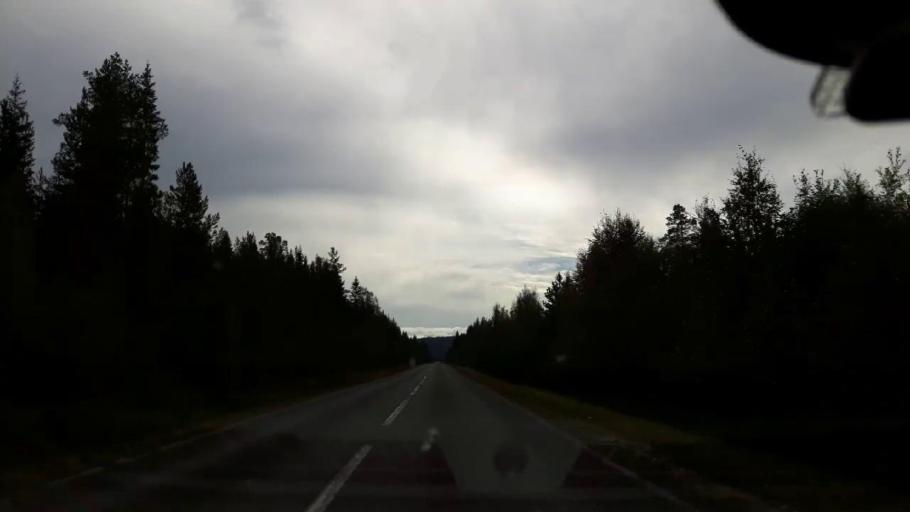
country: SE
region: Jaemtland
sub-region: Ragunda Kommun
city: Hammarstrand
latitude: 63.0595
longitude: 15.9267
